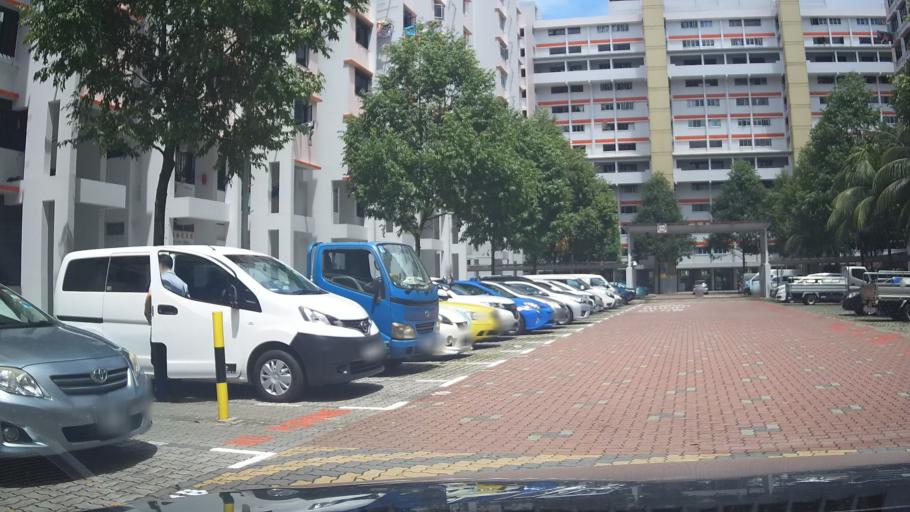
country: SG
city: Singapore
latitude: 1.3145
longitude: 103.8958
